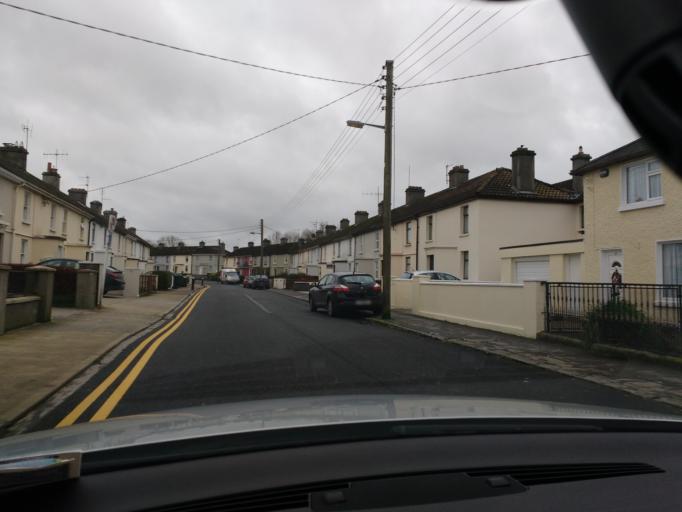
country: IE
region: Munster
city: Thurles
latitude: 52.6765
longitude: -7.8192
